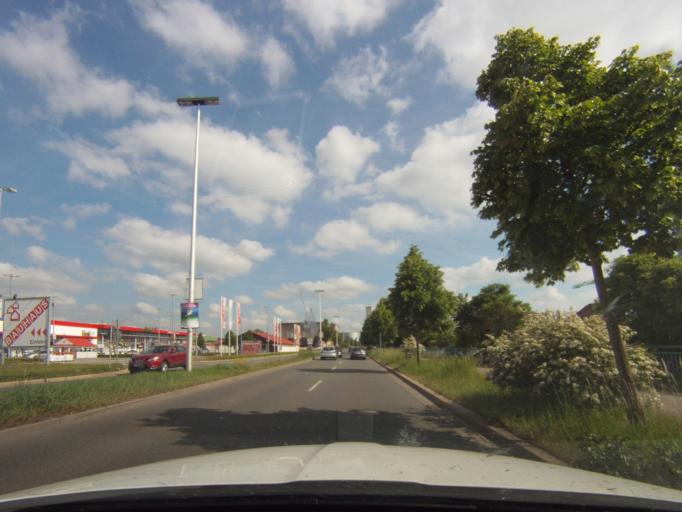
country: DE
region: Thuringia
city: Gera
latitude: 50.8682
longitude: 12.0767
